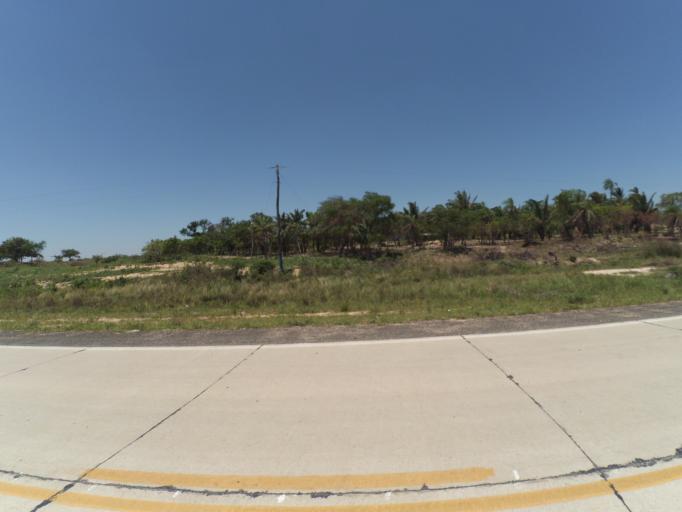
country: BO
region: Santa Cruz
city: Santa Cruz de la Sierra
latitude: -17.8057
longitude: -63.2807
